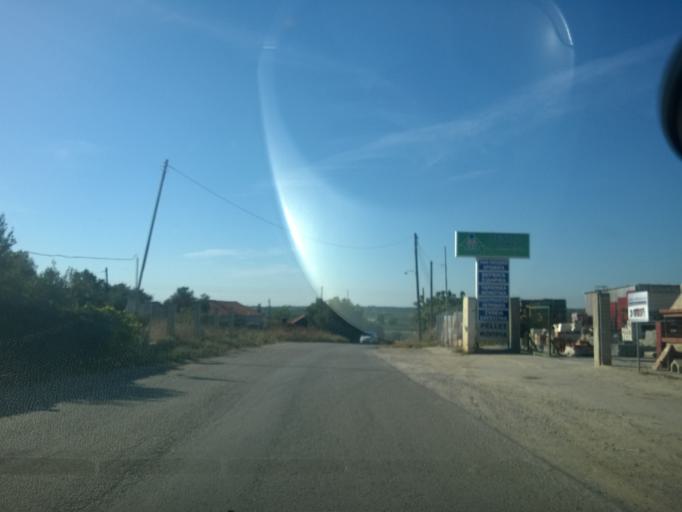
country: GR
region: Central Macedonia
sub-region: Nomos Chalkidikis
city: Nea Kallikrateia
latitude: 40.3378
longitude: 23.0504
